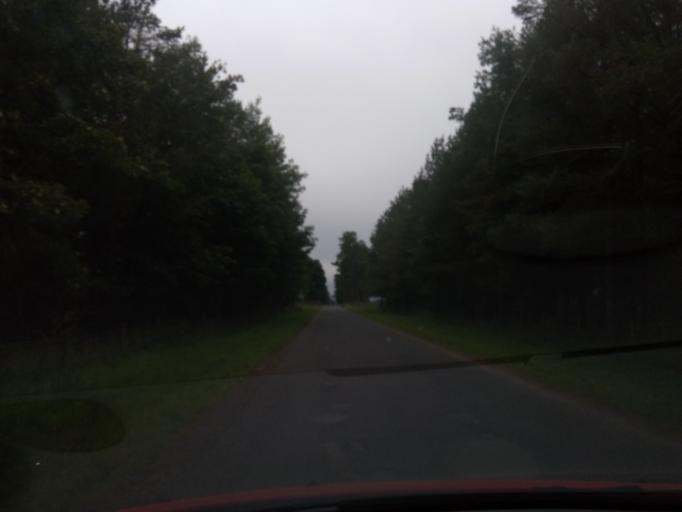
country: GB
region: England
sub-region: Northumberland
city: Otterburn
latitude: 55.2625
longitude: -2.1225
